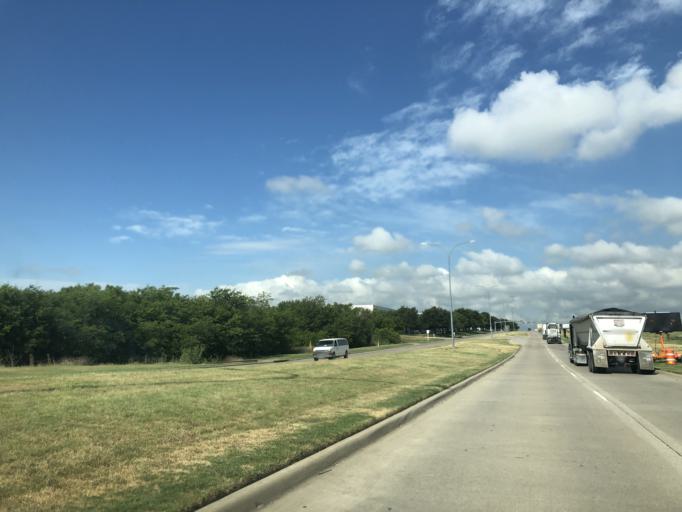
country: US
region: Texas
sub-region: Tarrant County
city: Haslet
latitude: 32.9740
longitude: -97.3231
